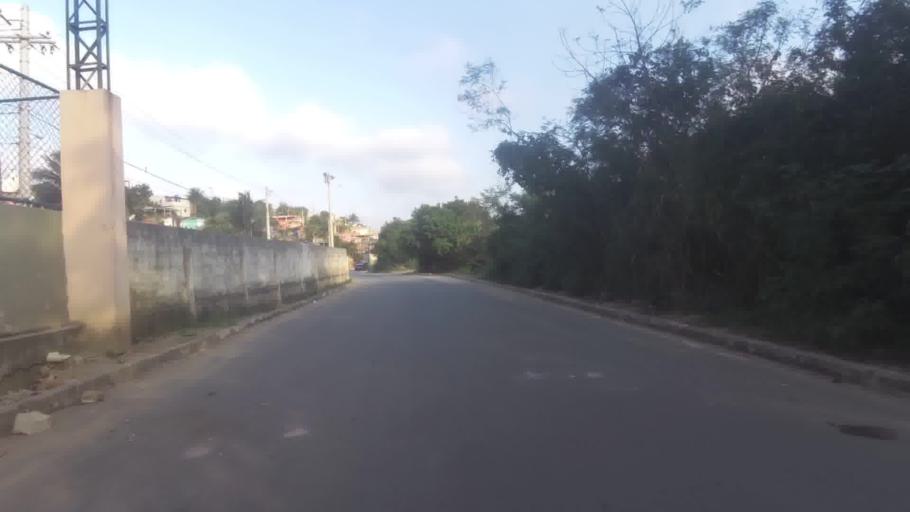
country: BR
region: Espirito Santo
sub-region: Itapemirim
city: Itapemirim
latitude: -21.0140
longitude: -40.8312
